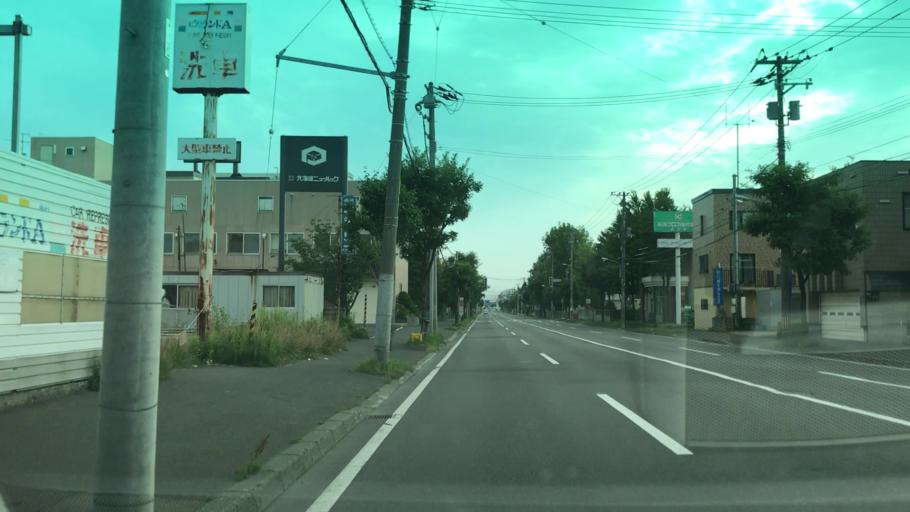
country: JP
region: Hokkaido
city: Sapporo
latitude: 43.0947
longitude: 141.3044
